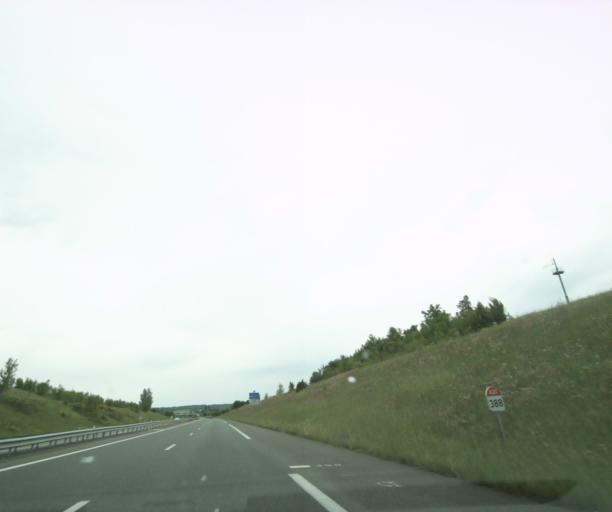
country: FR
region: Midi-Pyrenees
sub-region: Departement du Tarn-et-Garonne
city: Caussade
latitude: 44.2259
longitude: 1.5356
